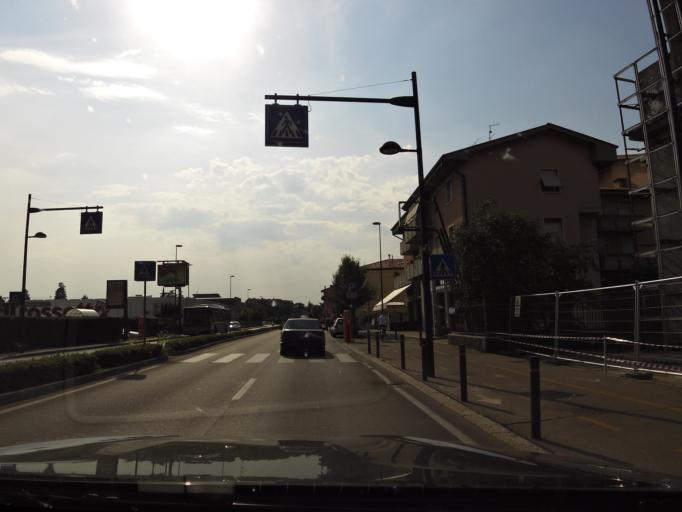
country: IT
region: Veneto
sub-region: Provincia di Verona
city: Verona
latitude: 45.4459
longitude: 10.9542
